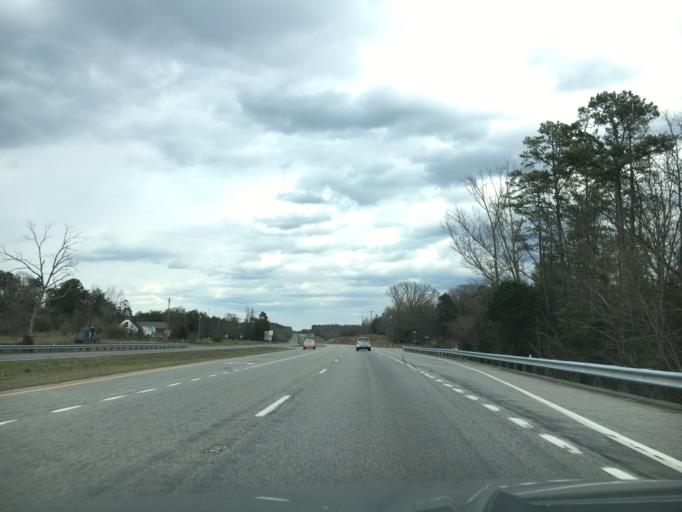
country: US
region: Virginia
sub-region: Mecklenburg County
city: Clarksville
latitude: 36.6380
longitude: -78.5212
